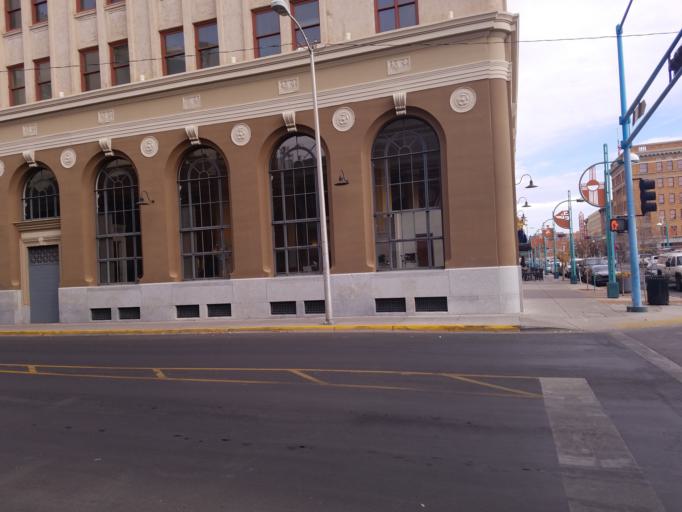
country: US
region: New Mexico
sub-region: Bernalillo County
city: Albuquerque
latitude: 35.0844
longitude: -106.6506
